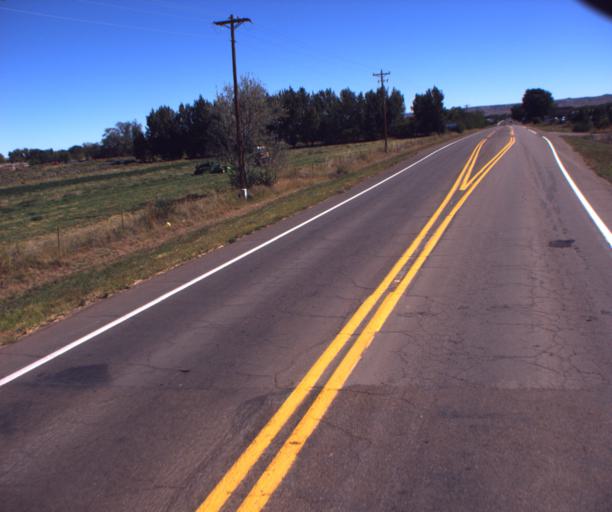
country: US
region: Arizona
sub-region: Apache County
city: Saint Johns
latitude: 34.5063
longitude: -109.3915
